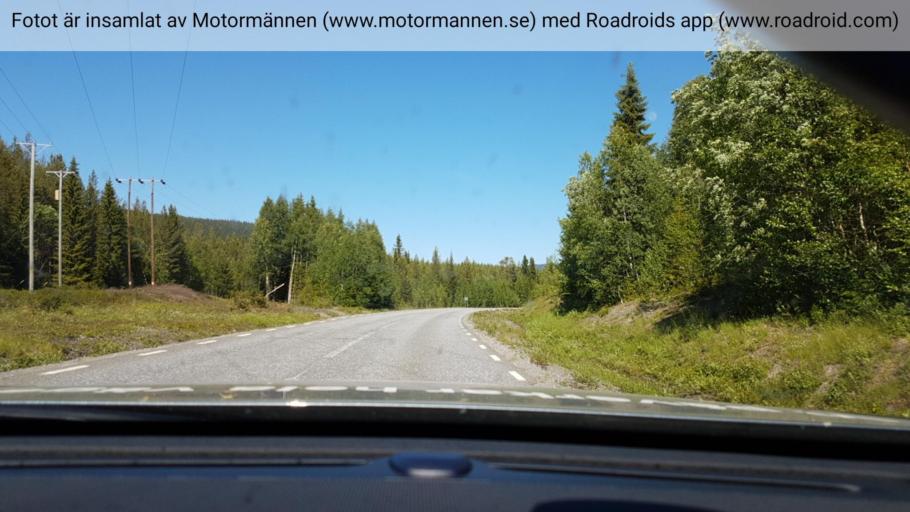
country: SE
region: Vaesterbotten
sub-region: Vilhelmina Kommun
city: Sjoberg
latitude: 64.8958
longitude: 15.8580
